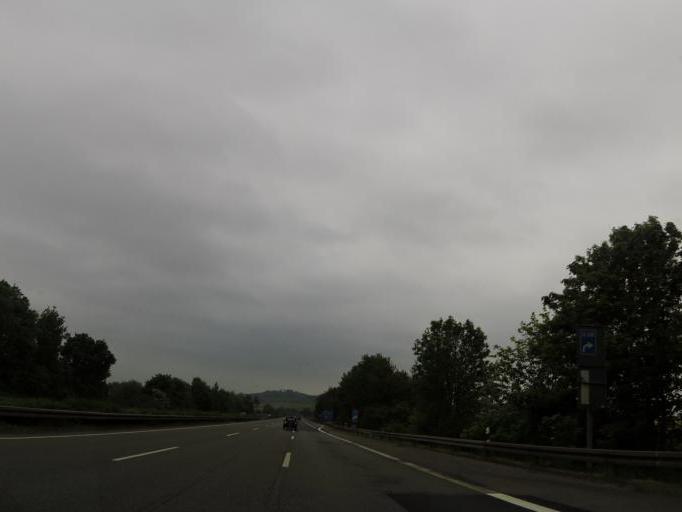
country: DE
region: Lower Saxony
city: Hillerse
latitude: 51.7063
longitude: 9.9381
